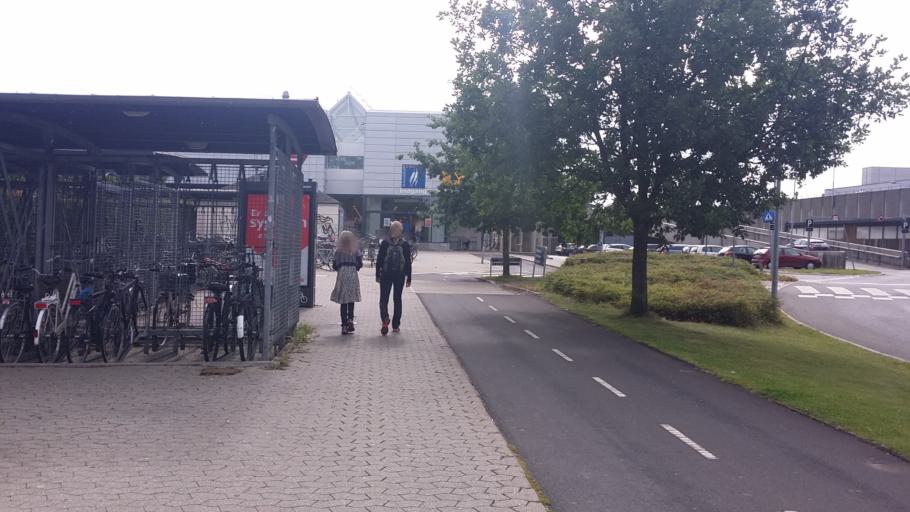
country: DK
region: Capital Region
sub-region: Ballerup Kommune
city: Ballerup
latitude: 55.7301
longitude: 12.3566
